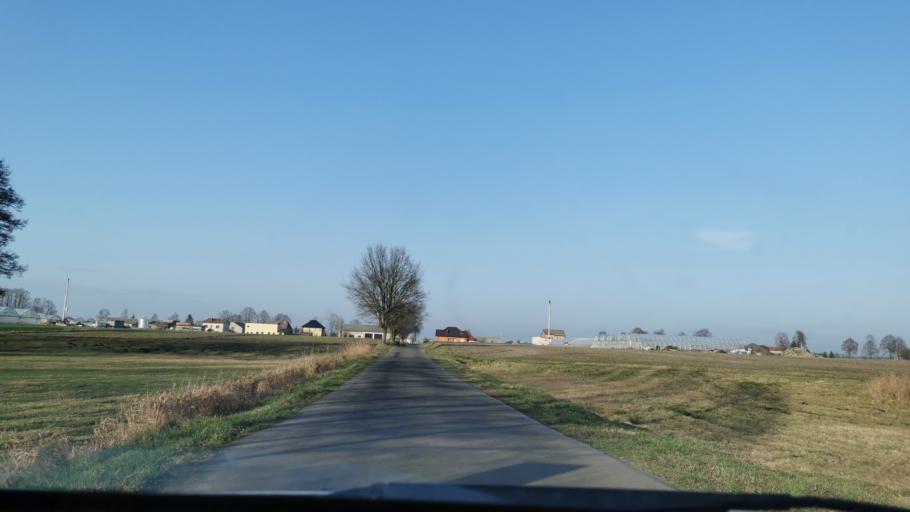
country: PL
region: Greater Poland Voivodeship
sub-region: Powiat kaliski
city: Opatowek
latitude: 51.6694
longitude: 18.2793
